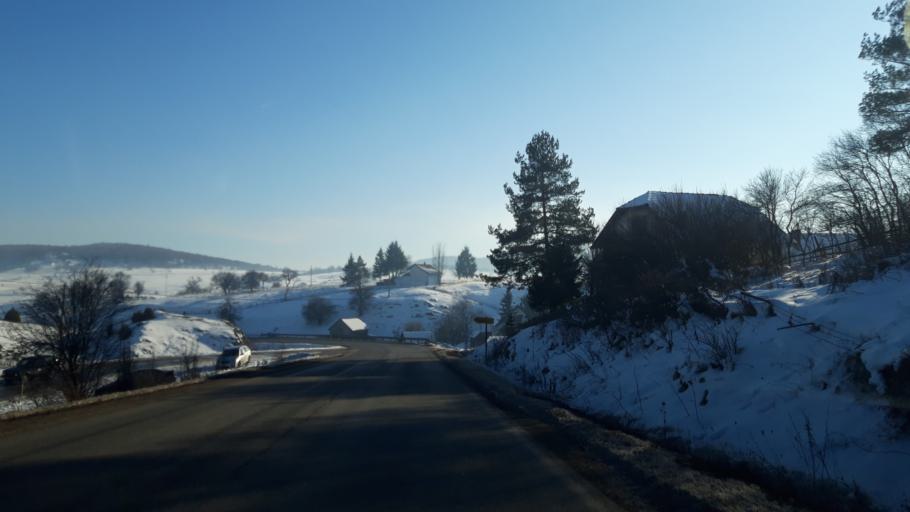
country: BA
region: Republika Srpska
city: Sokolac
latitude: 43.9212
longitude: 18.7571
